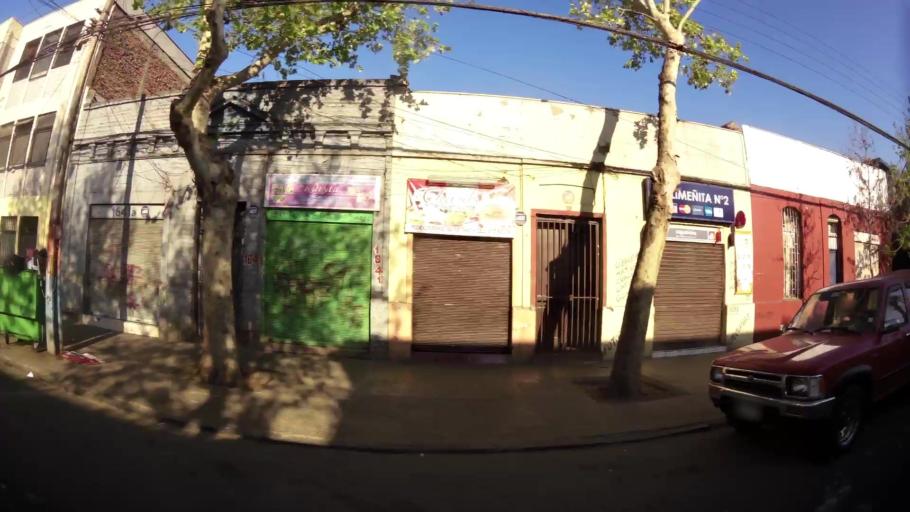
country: CL
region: Santiago Metropolitan
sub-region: Provincia de Santiago
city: Santiago
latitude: -33.4675
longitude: -70.6470
